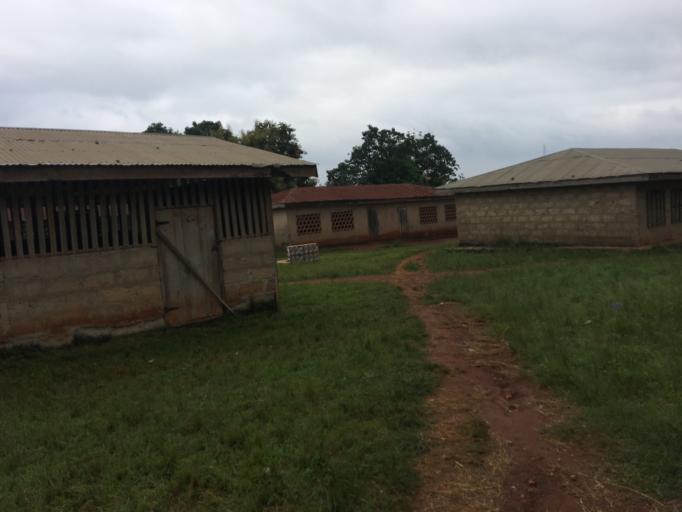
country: GH
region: Western
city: Bibiani
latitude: 6.8013
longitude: -2.5188
